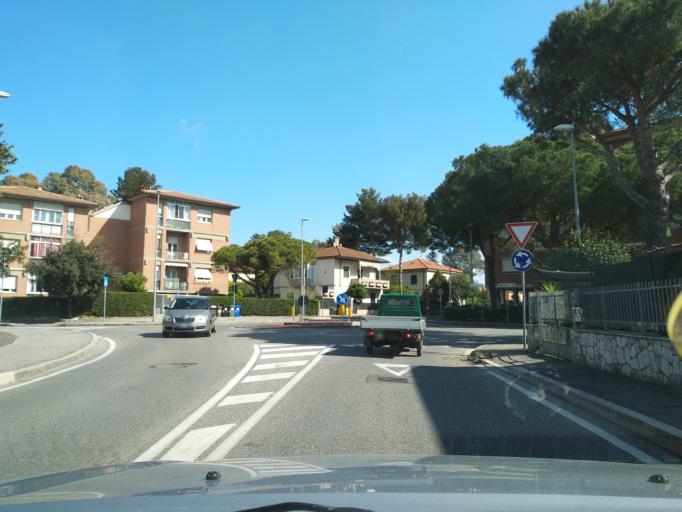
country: IT
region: Tuscany
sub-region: Provincia di Livorno
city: Livorno
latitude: 43.5402
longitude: 10.3408
